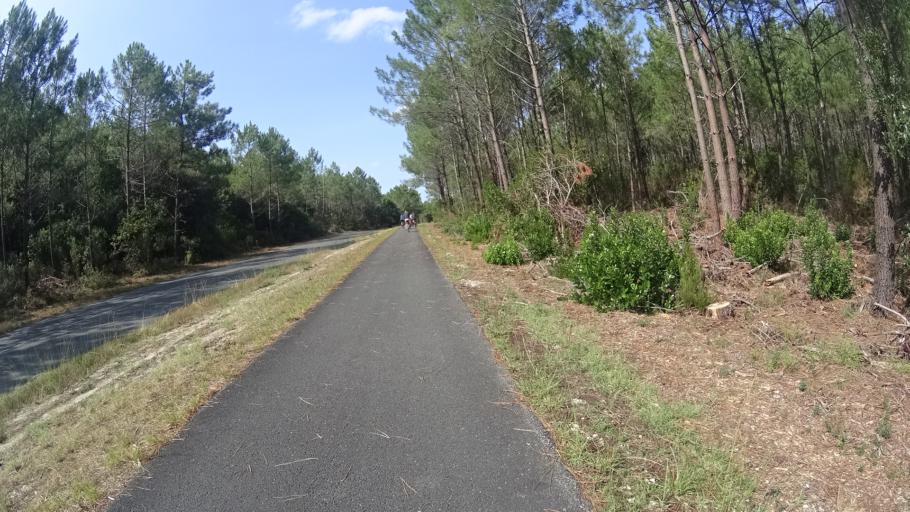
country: FR
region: Aquitaine
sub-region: Departement de la Gironde
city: Lacanau
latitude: 44.9827
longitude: -1.1432
